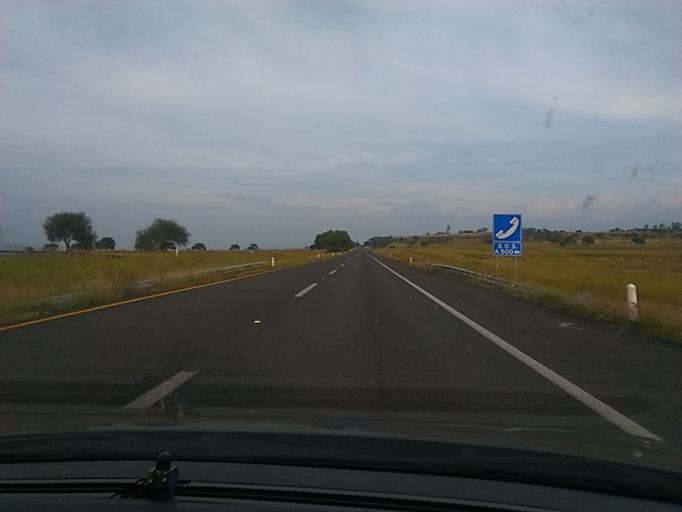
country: MX
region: Michoacan
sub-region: Alvaro Obregon
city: Lazaro Cardenas (La Purisima)
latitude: 19.8924
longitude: -101.0615
